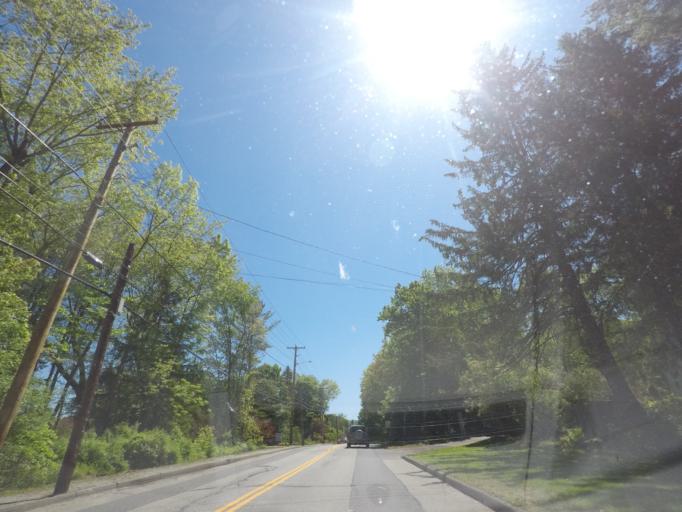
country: US
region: Maine
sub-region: Kennebec County
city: Augusta
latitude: 44.3193
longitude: -69.8087
